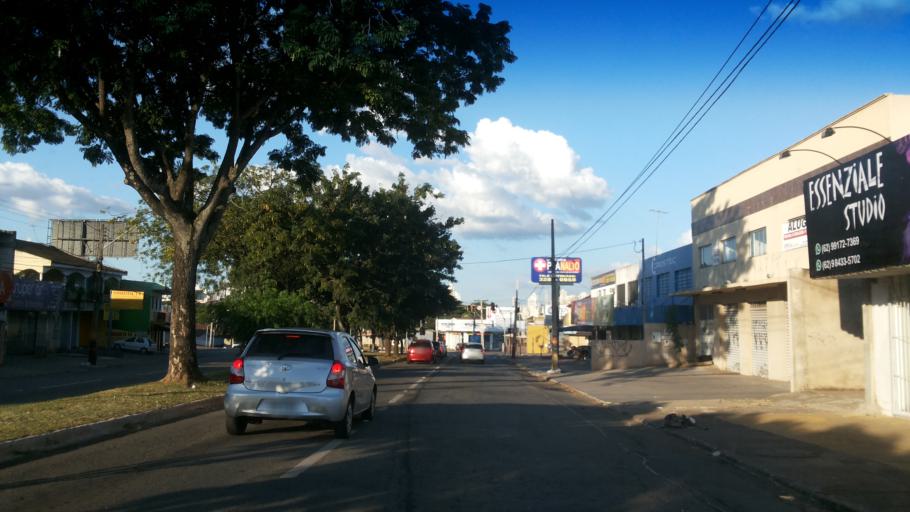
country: BR
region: Goias
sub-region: Goiania
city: Goiania
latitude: -16.7116
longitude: -49.3012
